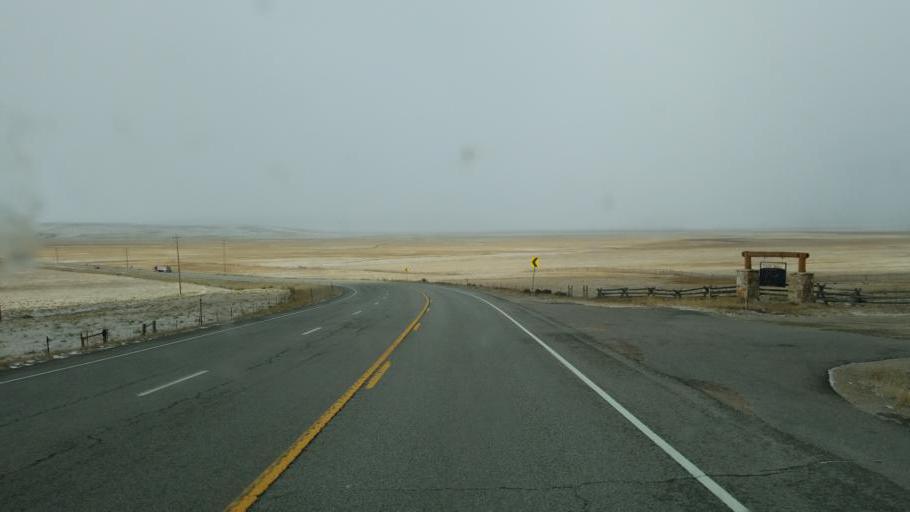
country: US
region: Colorado
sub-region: Summit County
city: Breckenridge
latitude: 39.4061
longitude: -105.7762
